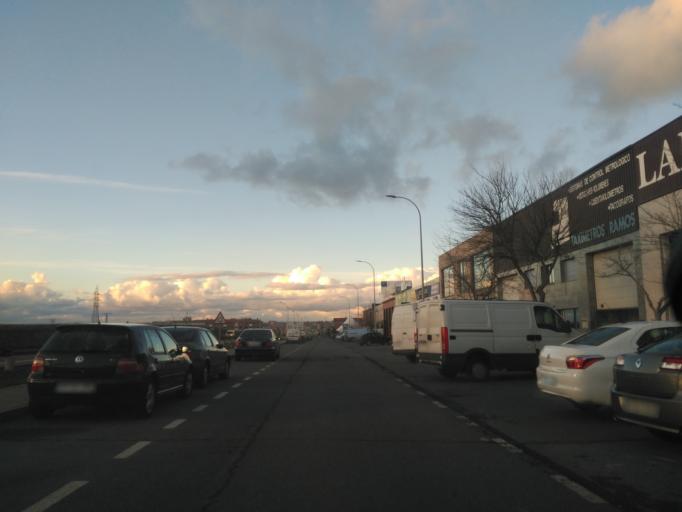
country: ES
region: Castille and Leon
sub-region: Provincia de Salamanca
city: Carbajosa de la Sagrada
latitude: 40.9380
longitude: -5.6682
